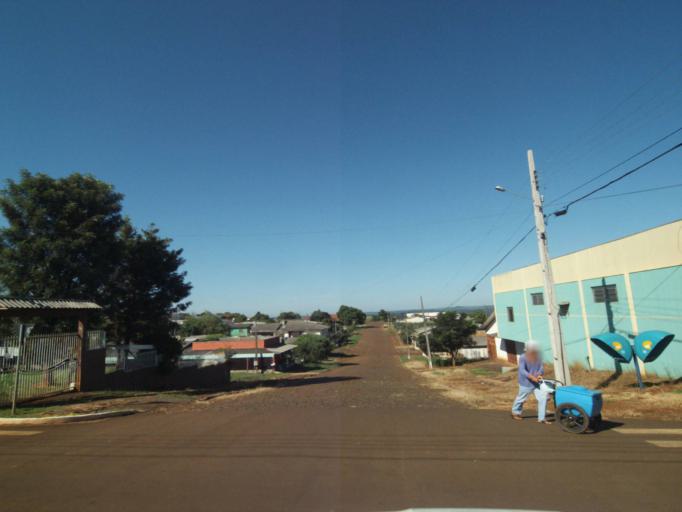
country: BR
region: Parana
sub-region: Laranjeiras Do Sul
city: Laranjeiras do Sul
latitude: -25.4940
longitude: -52.5338
